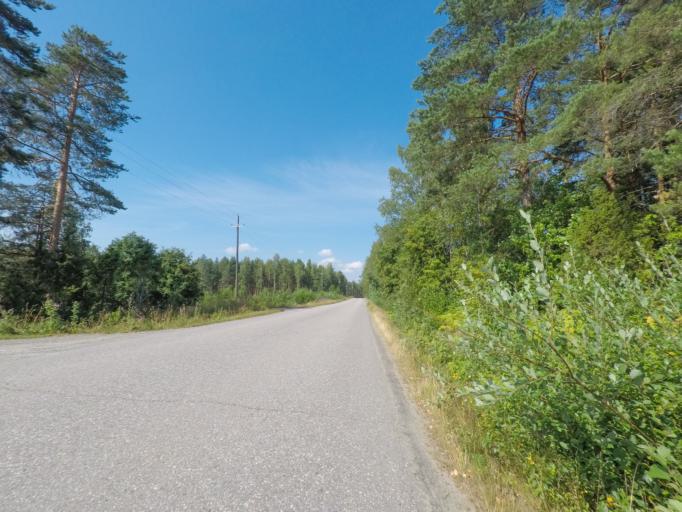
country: FI
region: Southern Savonia
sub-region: Mikkeli
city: Puumala
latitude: 61.4465
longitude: 28.1604
